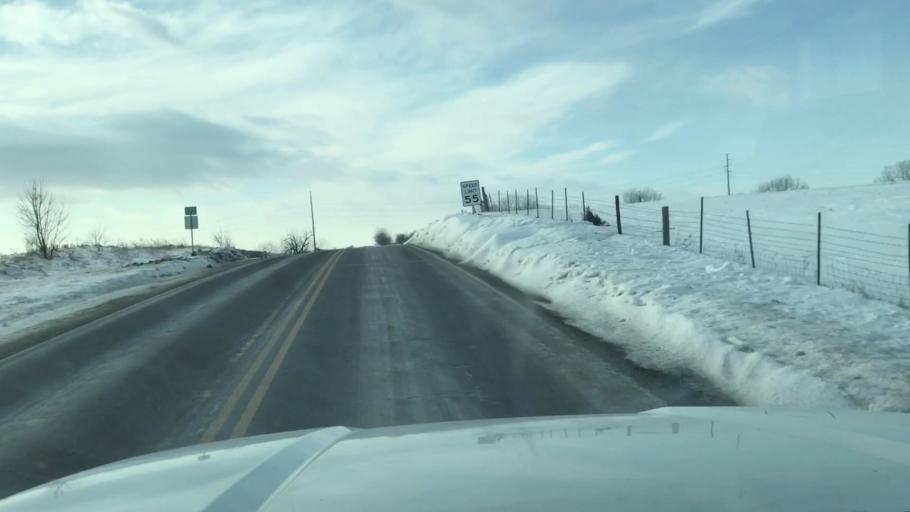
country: US
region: Missouri
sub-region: Nodaway County
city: Maryville
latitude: 40.2004
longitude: -94.8707
